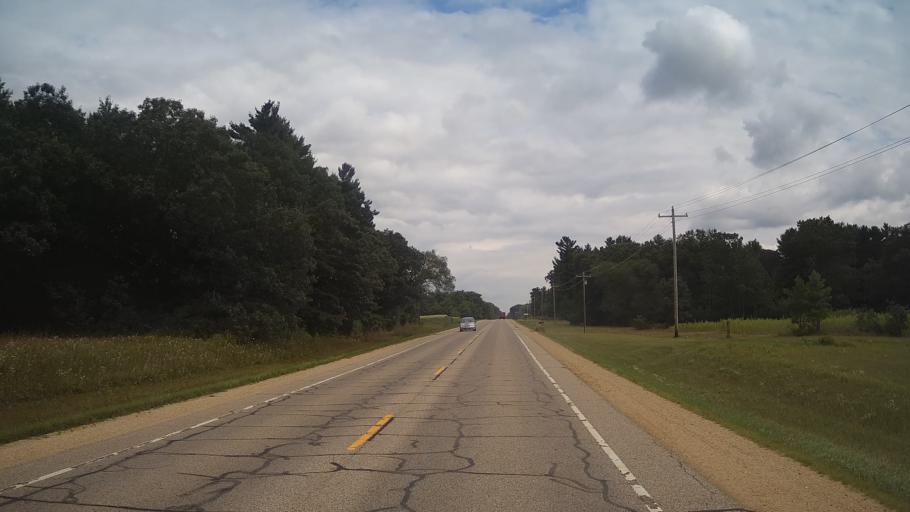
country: US
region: Wisconsin
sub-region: Waushara County
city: Wautoma
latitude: 44.0684
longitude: -89.3333
